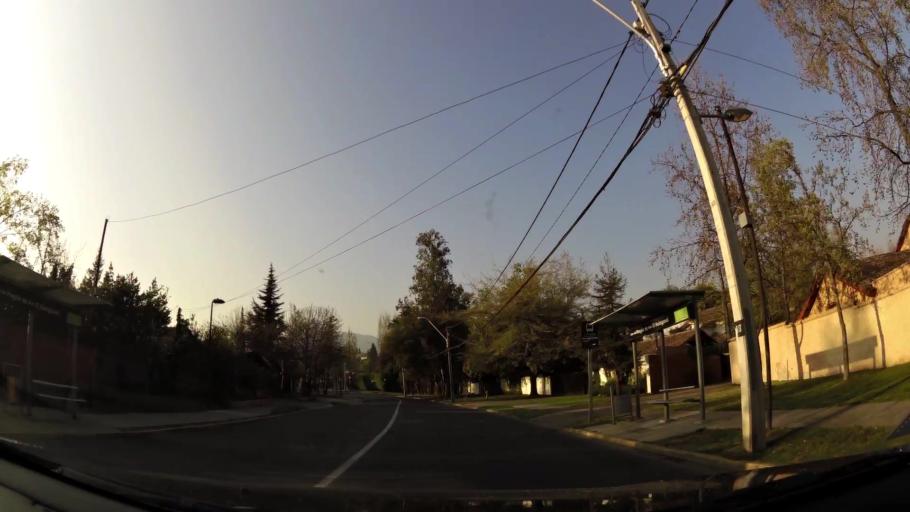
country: CL
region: Santiago Metropolitan
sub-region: Provincia de Santiago
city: Villa Presidente Frei, Nunoa, Santiago, Chile
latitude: -33.3455
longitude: -70.5095
